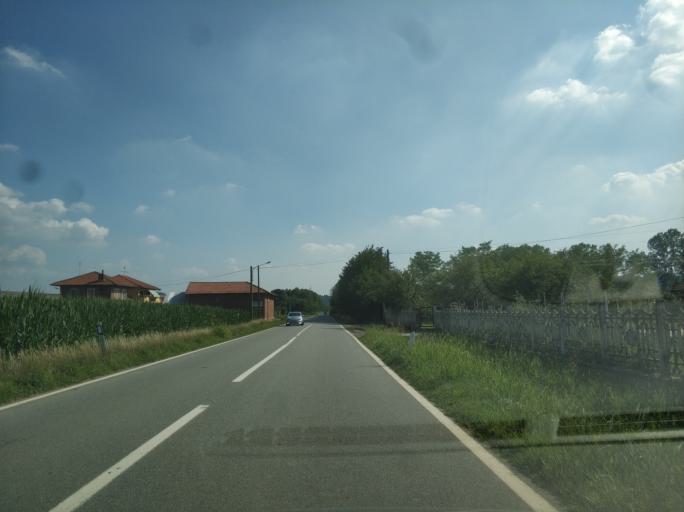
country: IT
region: Piedmont
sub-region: Provincia di Torino
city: Front
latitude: 45.2966
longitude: 7.6744
